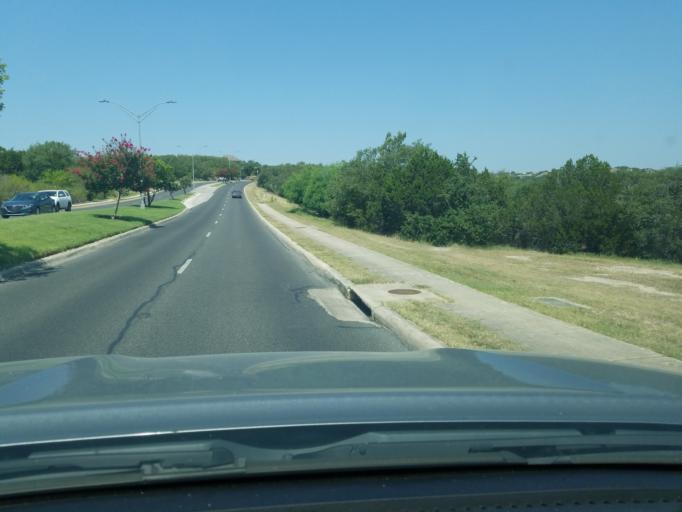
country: US
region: Texas
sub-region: Bexar County
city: Hollywood Park
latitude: 29.6390
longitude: -98.4768
